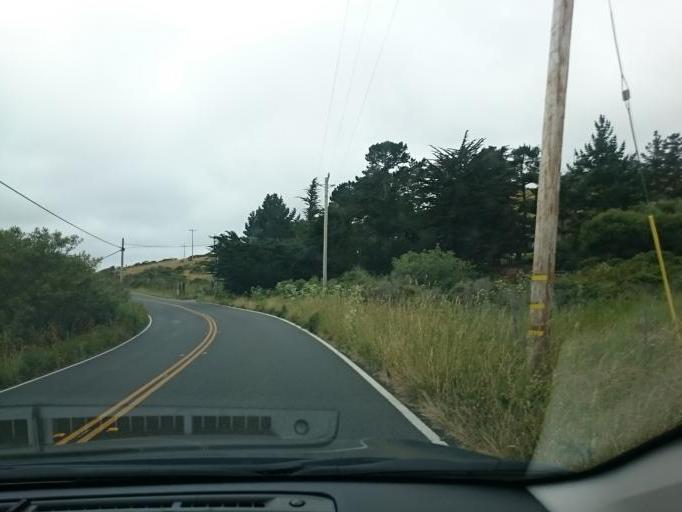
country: US
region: California
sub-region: Marin County
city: Inverness
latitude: 38.1765
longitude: -122.9013
